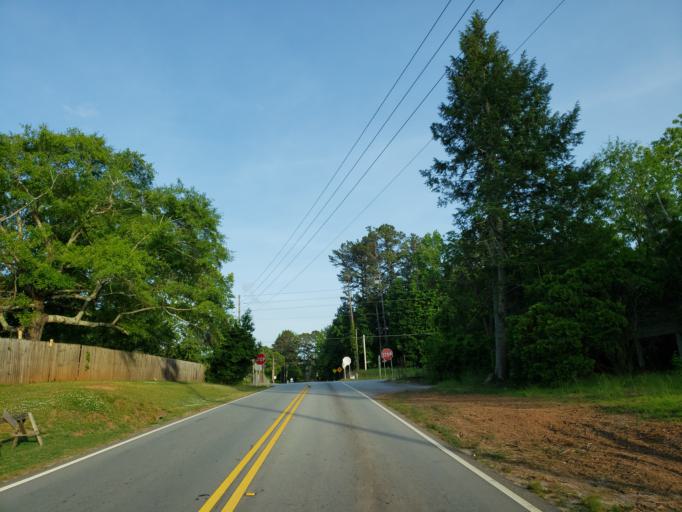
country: US
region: Georgia
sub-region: Carroll County
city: Carrollton
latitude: 33.5905
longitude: -85.1214
